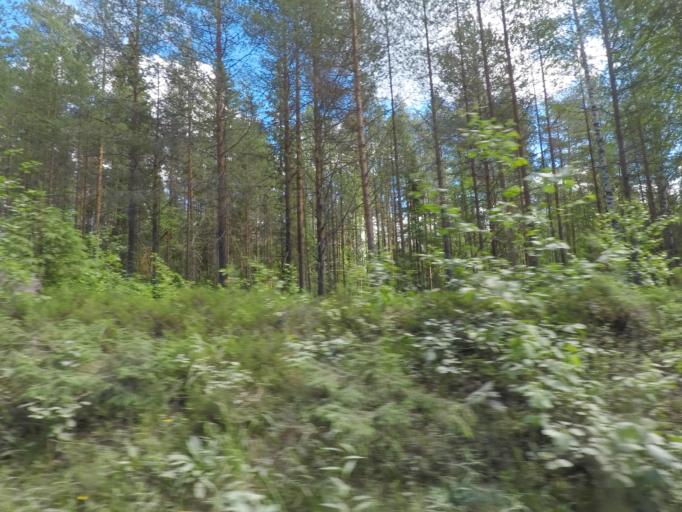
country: FI
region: Central Finland
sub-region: Jyvaeskylae
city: Hankasalmi
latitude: 62.4339
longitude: 26.6482
